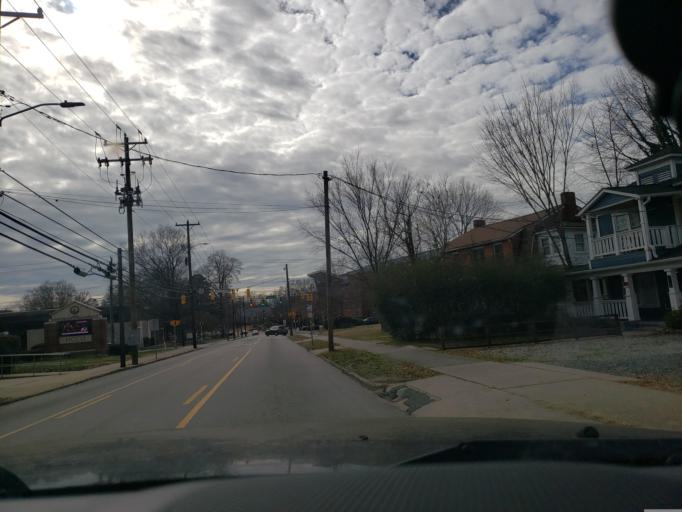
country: US
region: North Carolina
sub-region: Durham County
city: Durham
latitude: 35.9773
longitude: -78.9007
